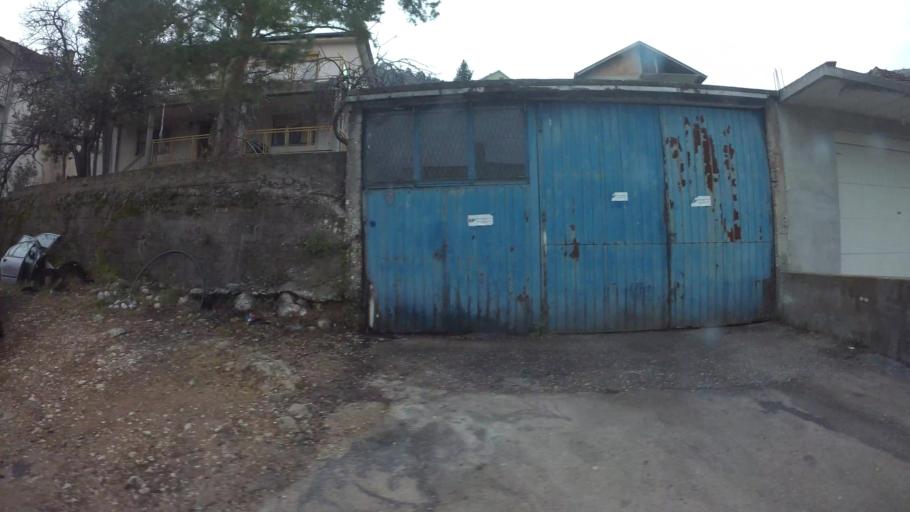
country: BA
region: Federation of Bosnia and Herzegovina
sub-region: Hercegovacko-Bosanski Kanton
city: Mostar
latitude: 43.3332
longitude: 17.7974
